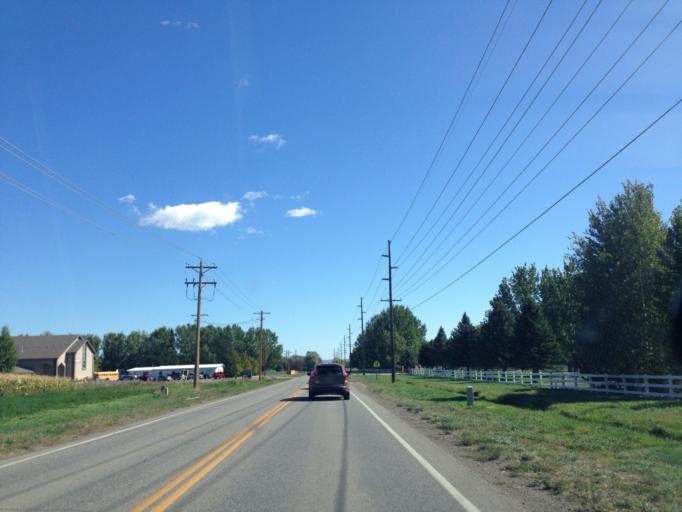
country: US
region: Montana
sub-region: Yellowstone County
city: Billings
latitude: 45.7840
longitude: -108.6330
